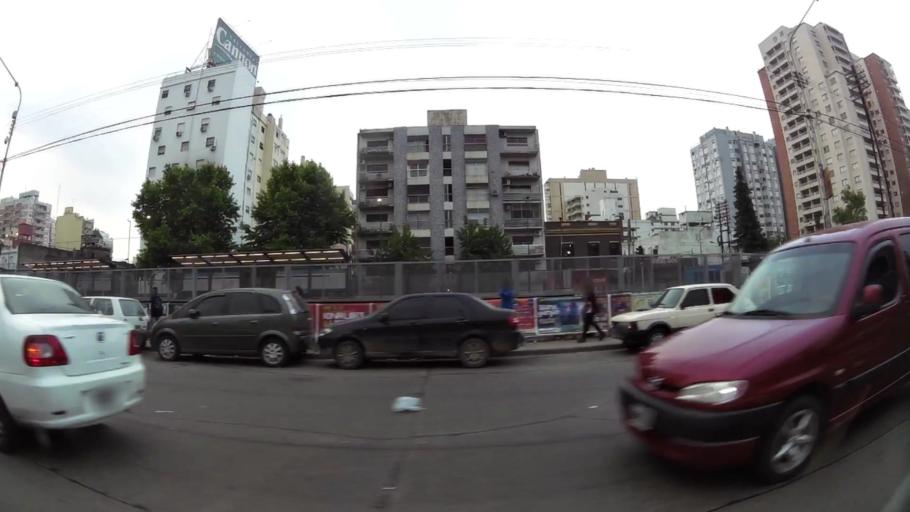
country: AR
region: Buenos Aires
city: San Justo
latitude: -34.6400
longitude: -58.5615
